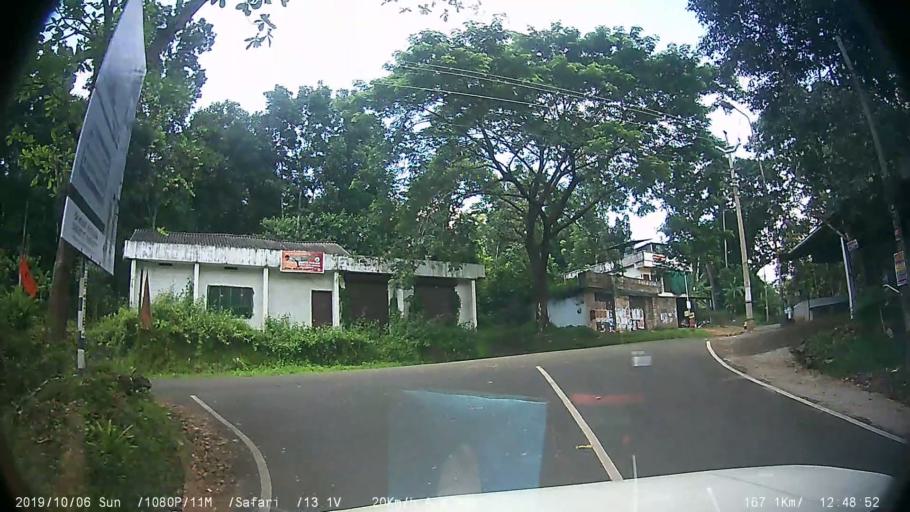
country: IN
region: Kerala
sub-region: Kottayam
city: Palackattumala
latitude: 9.7819
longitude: 76.5975
